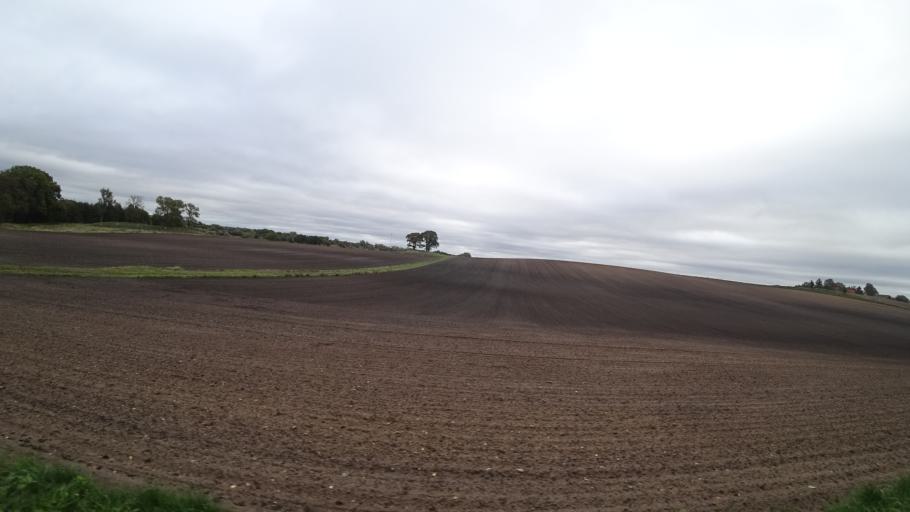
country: SE
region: Skane
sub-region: Kavlinge Kommun
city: Kaevlinge
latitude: 55.7883
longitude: 13.1383
